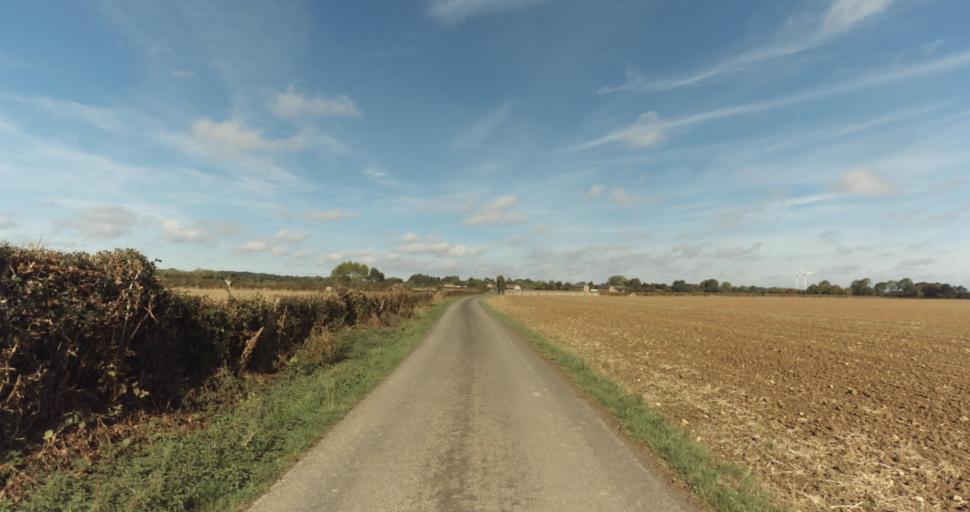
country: FR
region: Lower Normandy
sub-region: Departement du Calvados
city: La Vespiere
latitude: 48.9295
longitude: 0.3484
